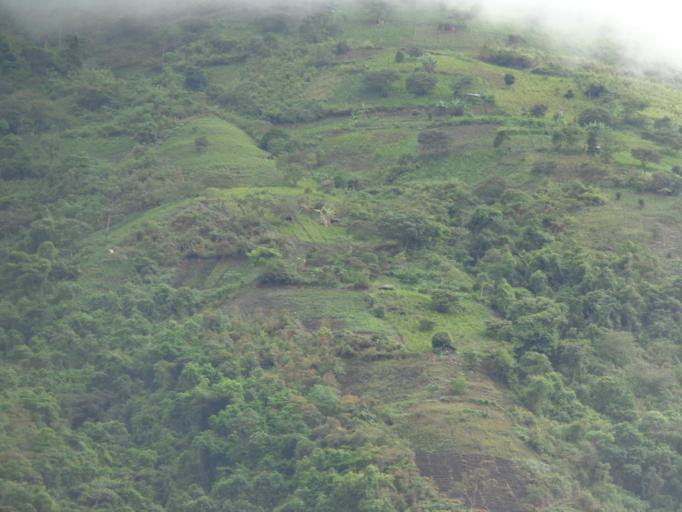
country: BO
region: La Paz
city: Coripata
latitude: -16.4024
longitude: -67.6541
